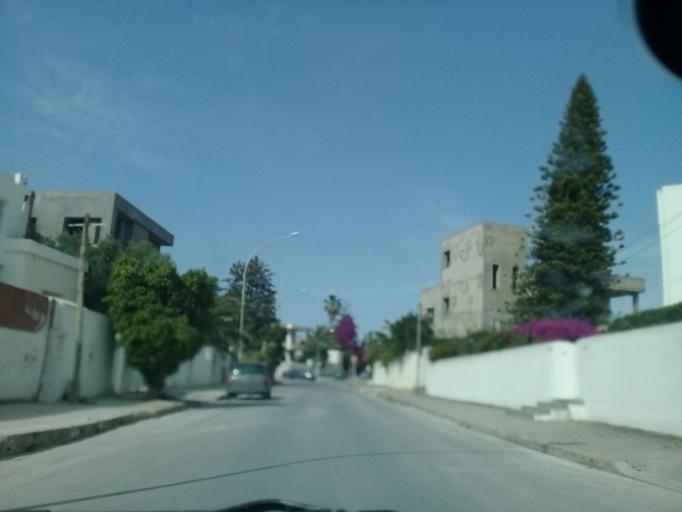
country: TN
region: Tunis
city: Tunis
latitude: 36.8492
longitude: 10.1594
